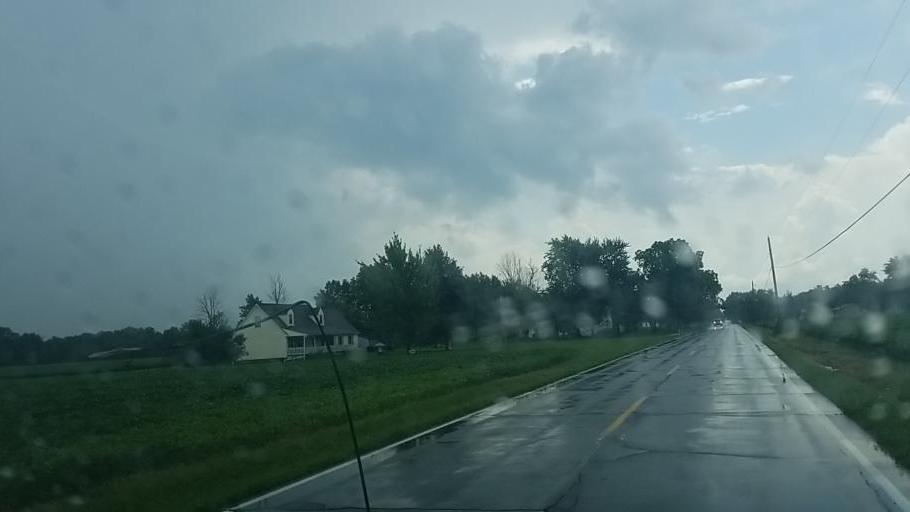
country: US
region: Ohio
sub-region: Lorain County
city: Grafton
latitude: 41.2496
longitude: -82.0835
